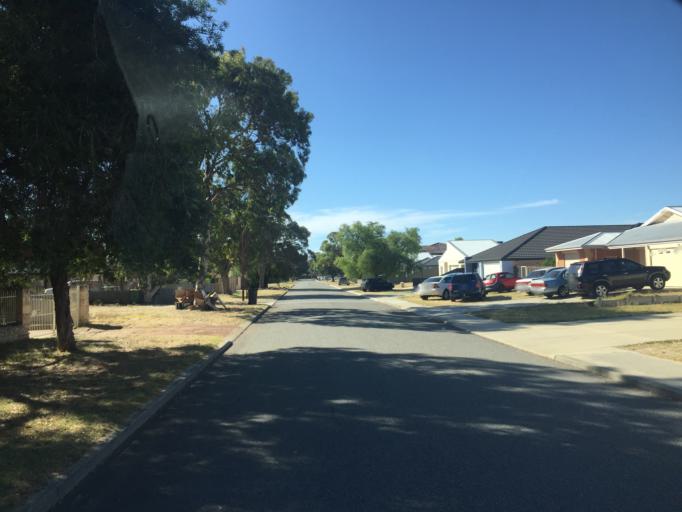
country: AU
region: Western Australia
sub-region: Gosnells
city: Gosnells
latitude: -32.0599
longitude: 116.0039
